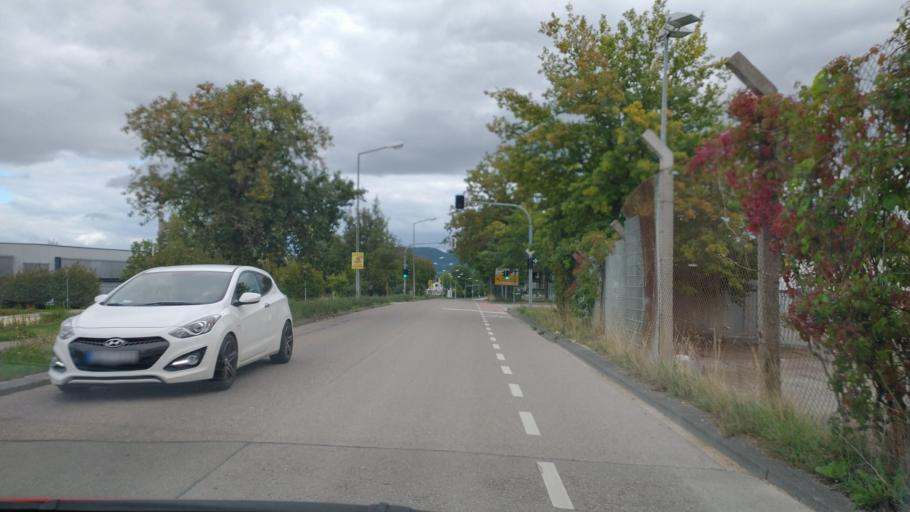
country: DE
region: Baden-Wuerttemberg
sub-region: Regierungsbezirk Stuttgart
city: Schwabisch Gmund
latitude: 48.7939
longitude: 9.8237
